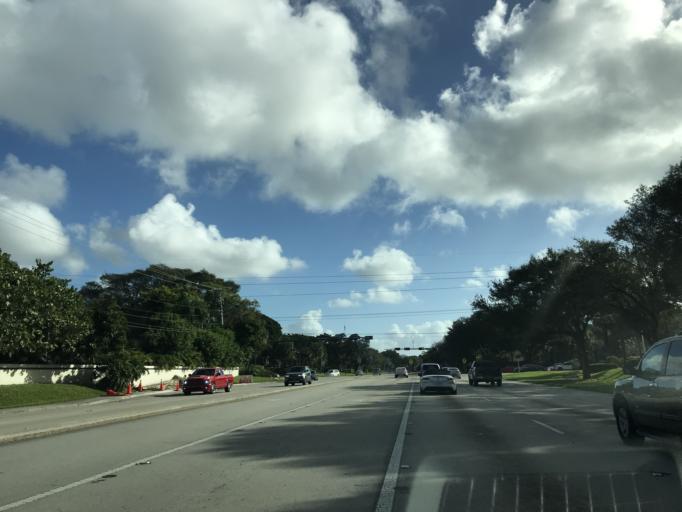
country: US
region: Florida
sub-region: Broward County
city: Coconut Creek
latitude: 26.2597
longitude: -80.1875
